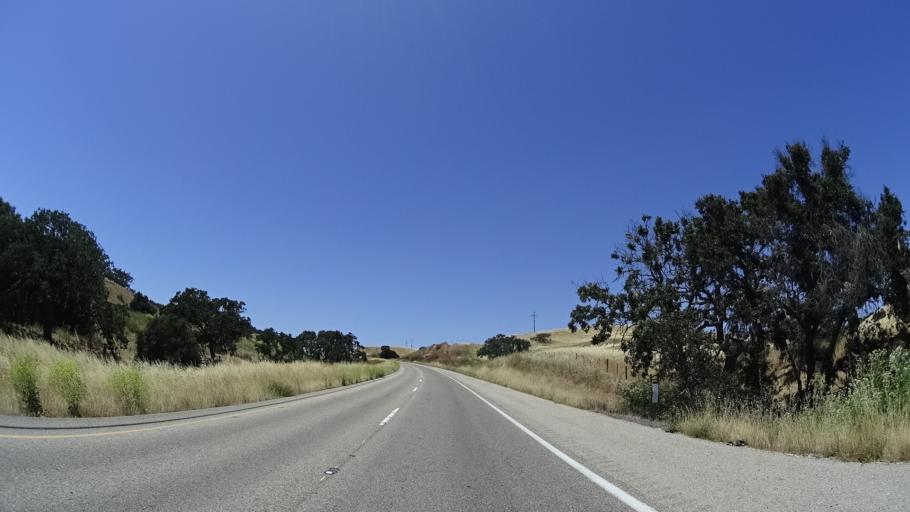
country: US
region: California
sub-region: Santa Barbara County
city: Los Olivos
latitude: 34.7067
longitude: -120.1708
